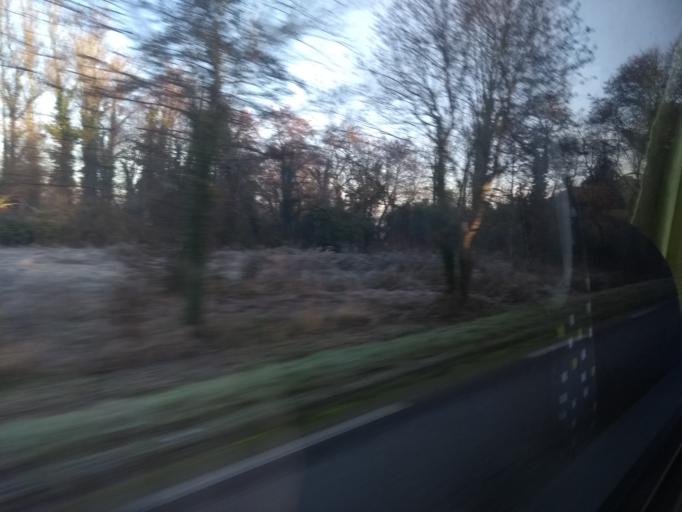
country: FR
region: Aquitaine
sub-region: Departement de la Gironde
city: Canejan
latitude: 44.7530
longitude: -0.6313
